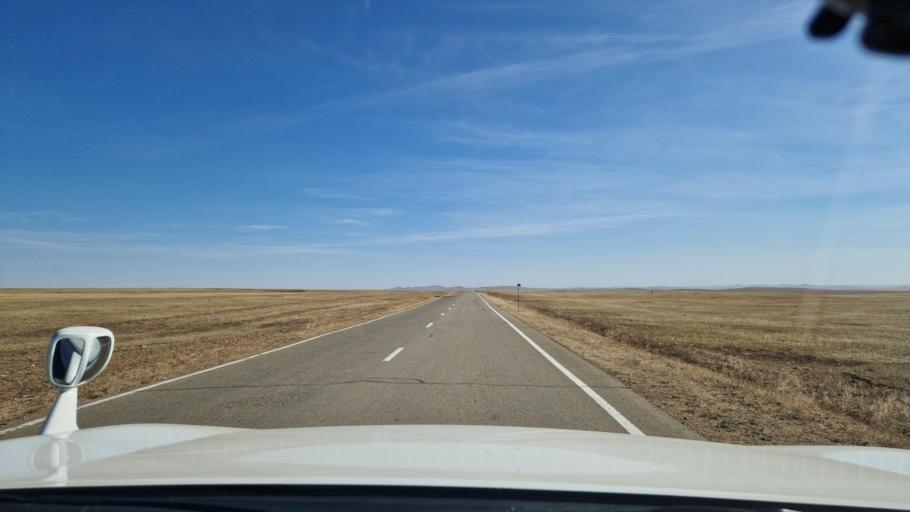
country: MN
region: Suhbaatar
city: Hanhohiy
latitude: 47.5682
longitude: 112.2886
